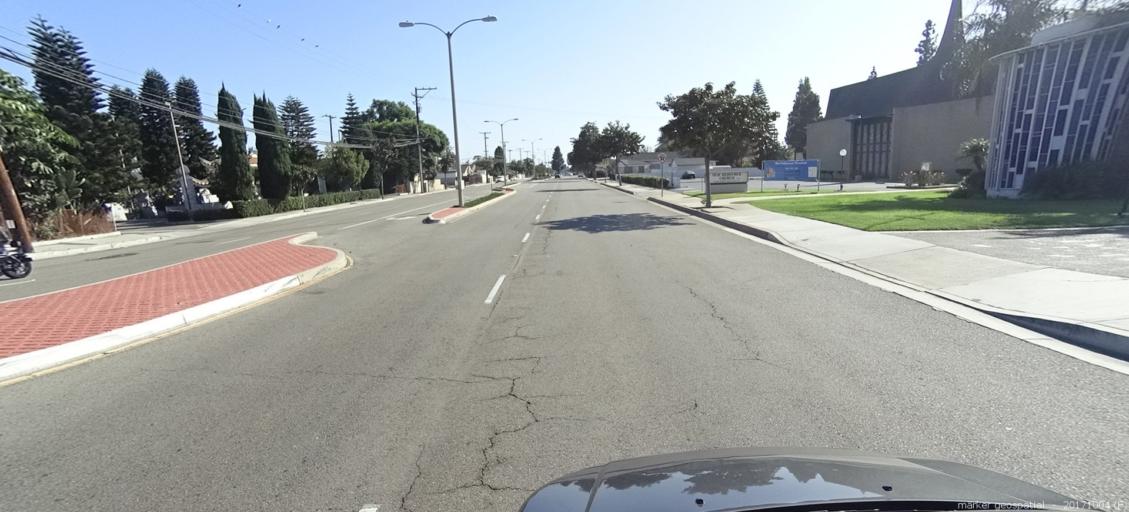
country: US
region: California
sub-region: Orange County
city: Stanton
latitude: 33.7840
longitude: -117.9754
